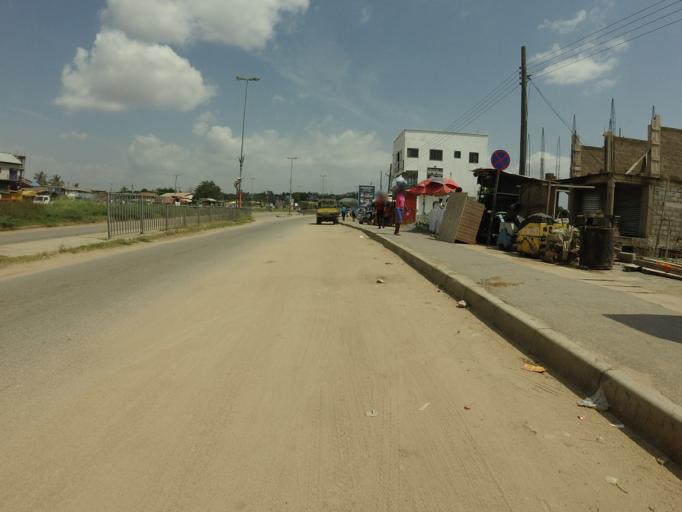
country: GH
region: Greater Accra
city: Gbawe
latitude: 5.6269
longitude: -0.3103
